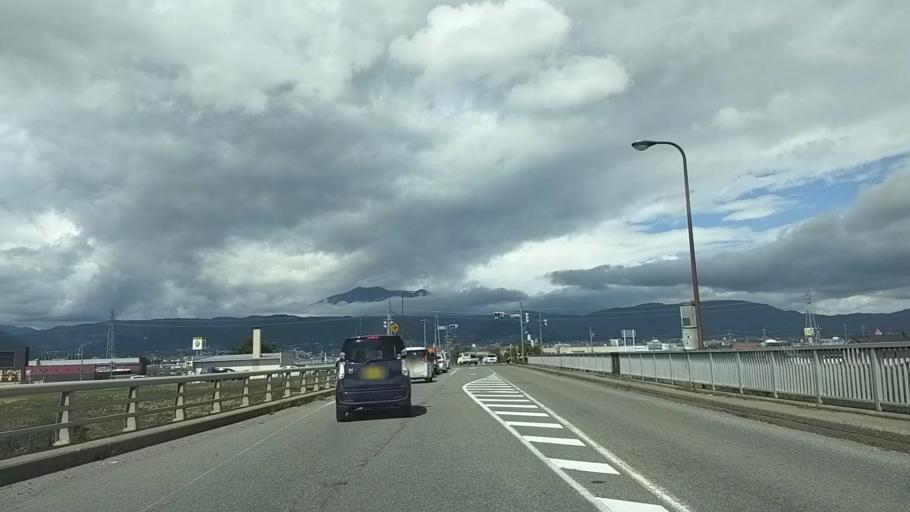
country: JP
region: Nagano
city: Nagano-shi
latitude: 36.6244
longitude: 138.2382
